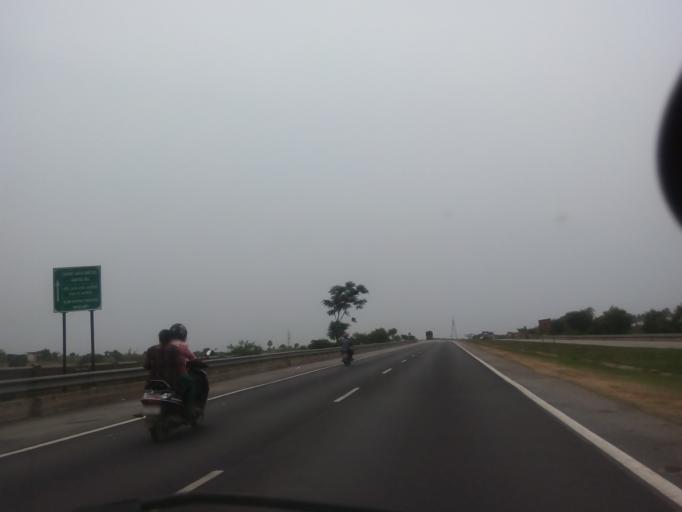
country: IN
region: Karnataka
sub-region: Bangalore Urban
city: Bangalore
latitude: 12.9074
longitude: 77.4686
